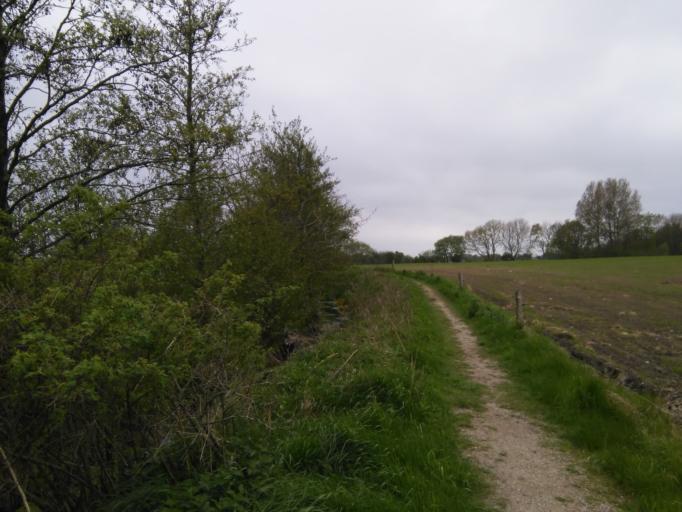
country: DK
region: Central Jutland
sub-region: Arhus Kommune
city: Beder
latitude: 56.0484
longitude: 10.2092
